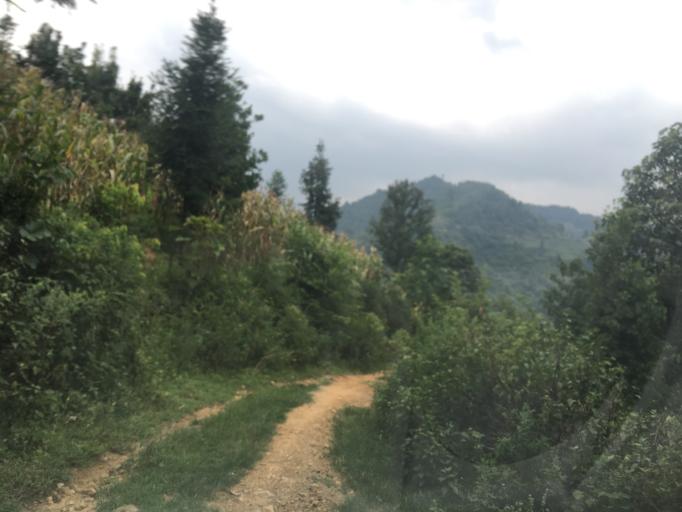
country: CN
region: Guangxi Zhuangzu Zizhiqu
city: Xinzhou
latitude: 25.1663
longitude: 105.6973
